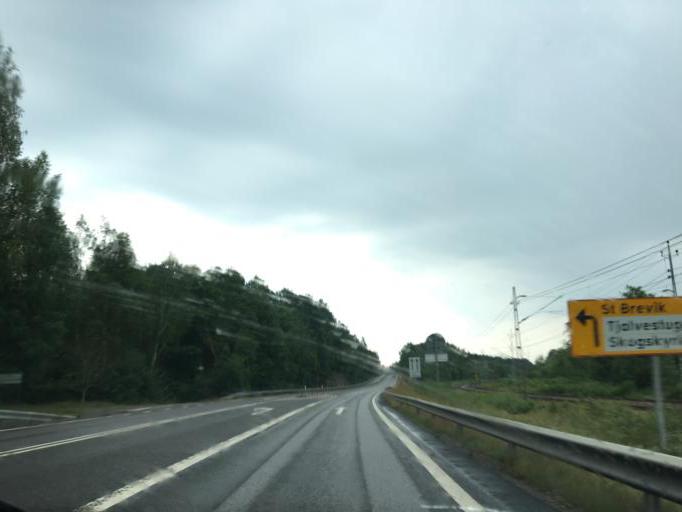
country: SE
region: OEstergoetland
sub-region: Norrkopings Kommun
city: Jursla
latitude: 58.7782
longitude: 16.1620
